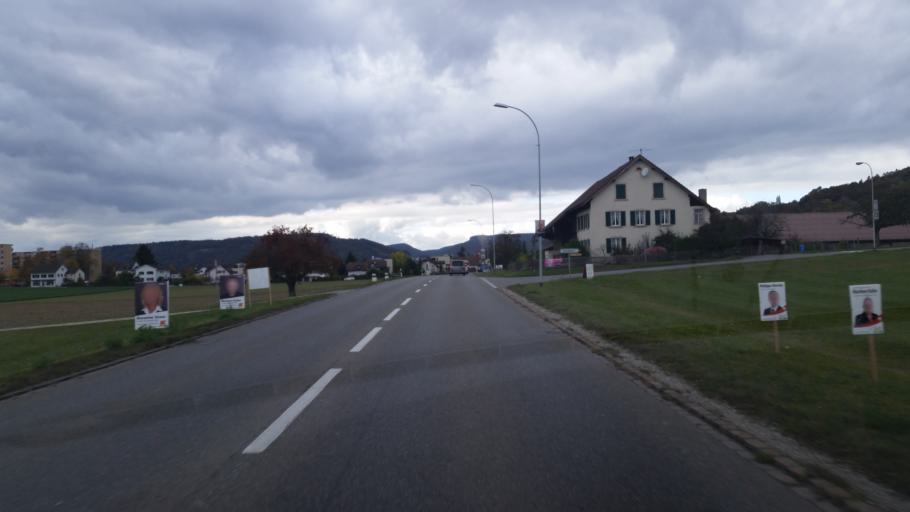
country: CH
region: Aargau
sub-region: Bezirk Baden
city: Turgi
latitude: 47.4944
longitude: 8.2729
